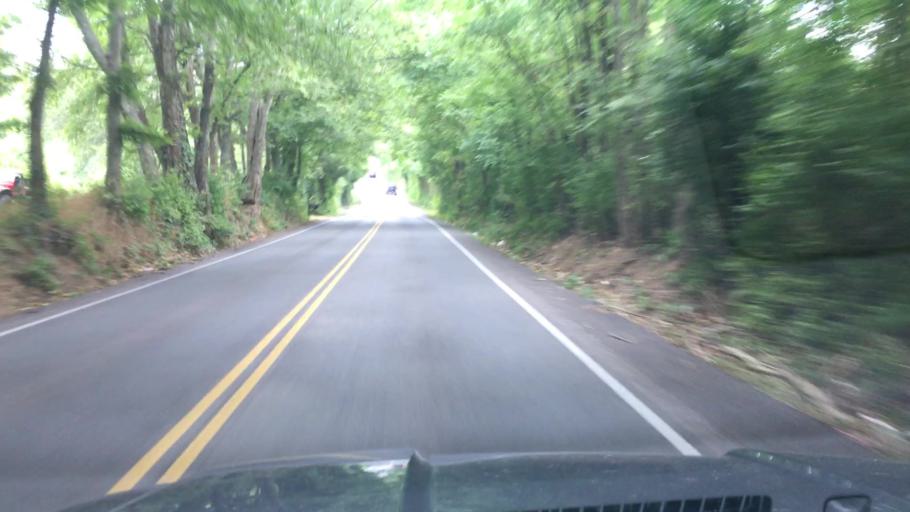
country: US
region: Tennessee
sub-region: Williamson County
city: Thompson's Station
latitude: 35.8047
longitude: -86.8627
